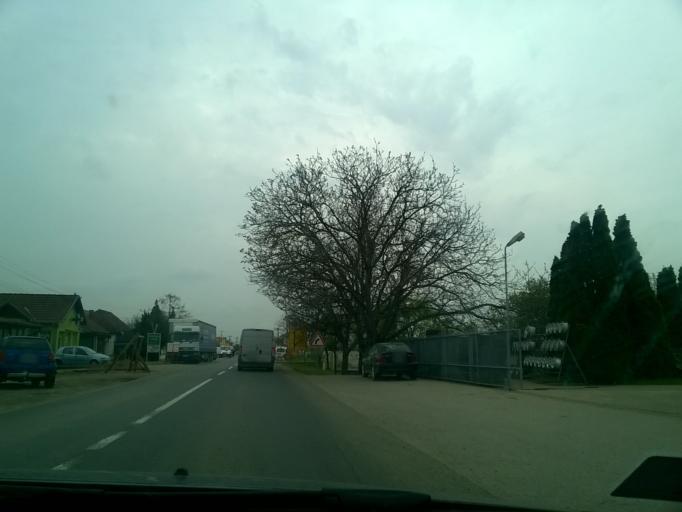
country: RS
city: Platicevo
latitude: 44.8254
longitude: 19.7799
